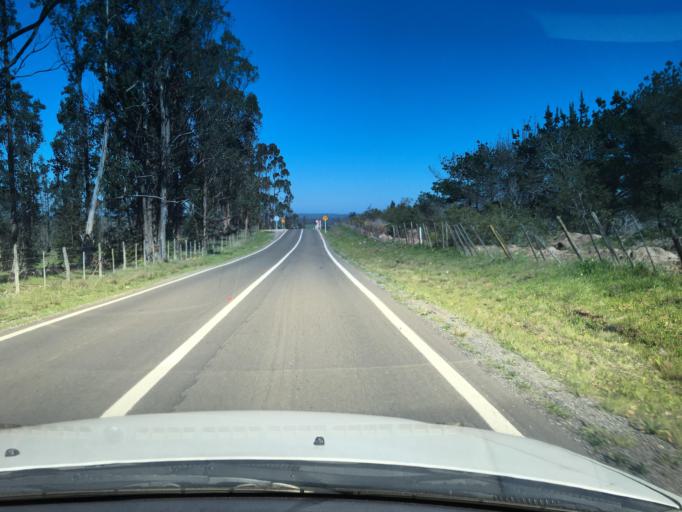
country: CL
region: Valparaiso
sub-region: San Antonio Province
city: El Tabo
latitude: -33.4076
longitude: -71.5896
